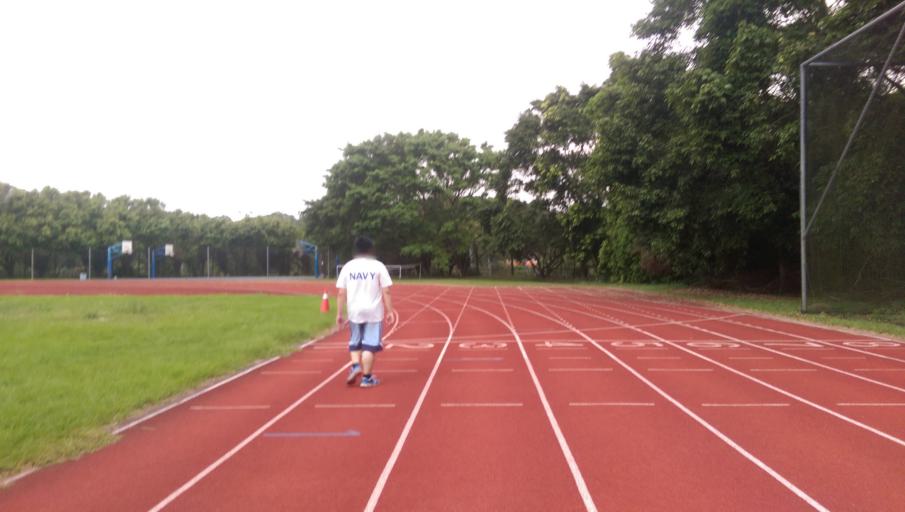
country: TW
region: Taiwan
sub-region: Hsinchu
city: Hsinchu
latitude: 24.7608
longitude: 120.9523
